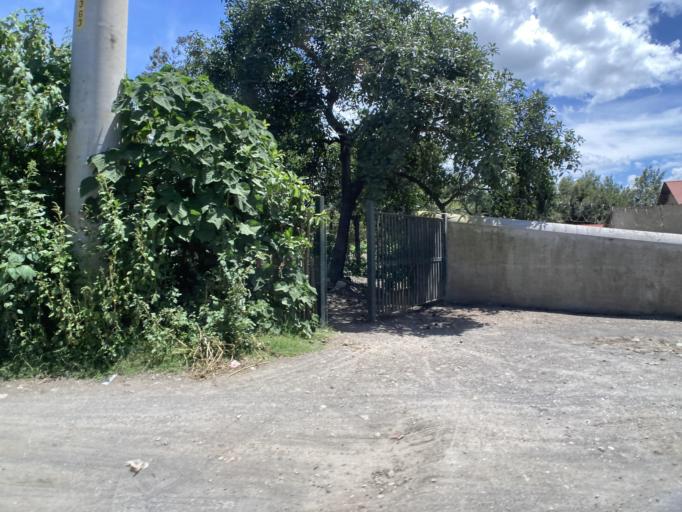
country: GT
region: Sacatepequez
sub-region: Municipio de Santa Maria de Jesus
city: Santa Maria de Jesus
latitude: 14.5384
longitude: -90.7352
